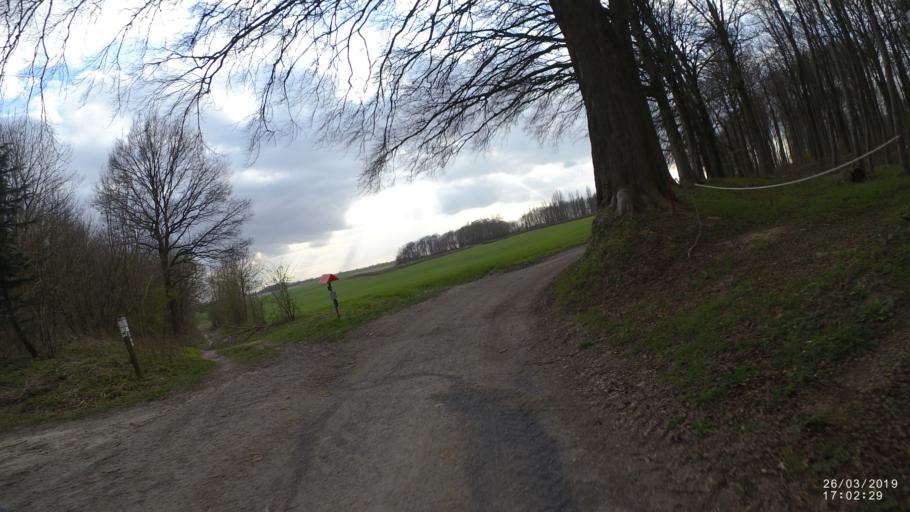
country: BE
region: Flanders
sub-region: Provincie Vlaams-Brabant
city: Huldenberg
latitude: 50.8319
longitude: 4.5963
